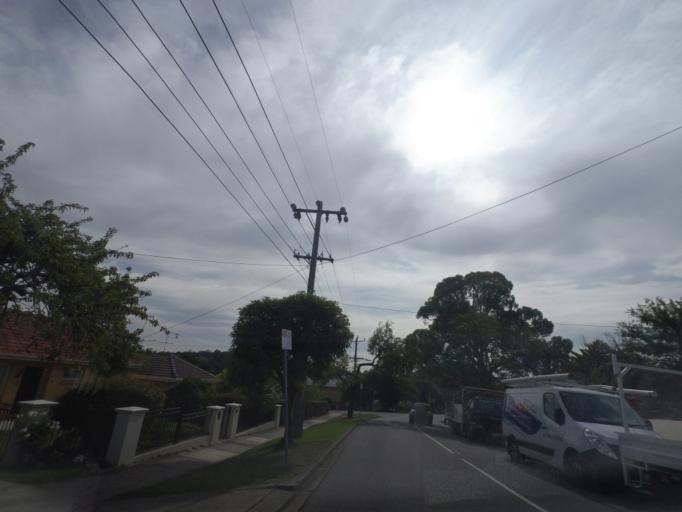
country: AU
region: Victoria
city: Rosanna
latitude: -37.7421
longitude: 145.0786
